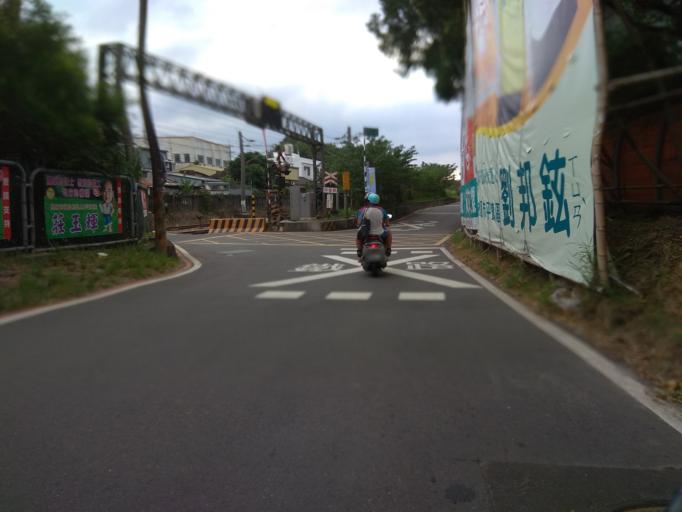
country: TW
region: Taiwan
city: Daxi
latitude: 24.9336
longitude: 121.2044
